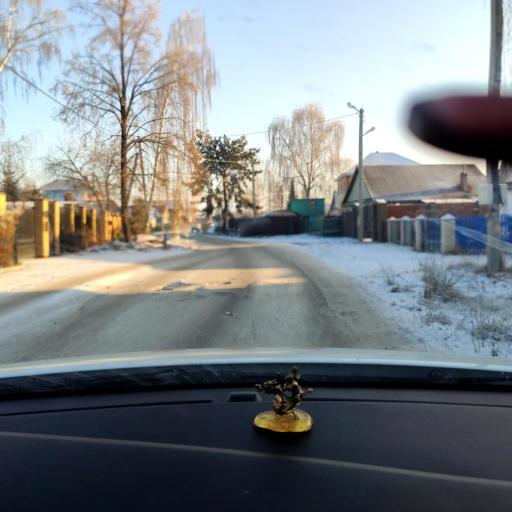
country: RU
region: Tatarstan
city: Stolbishchi
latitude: 55.6756
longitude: 49.1120
